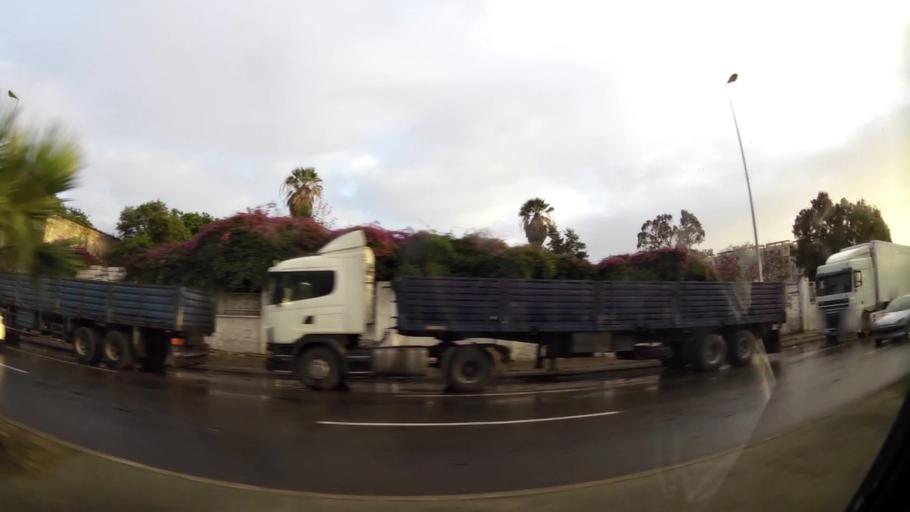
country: MA
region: Grand Casablanca
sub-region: Casablanca
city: Casablanca
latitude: 33.5867
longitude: -7.5885
